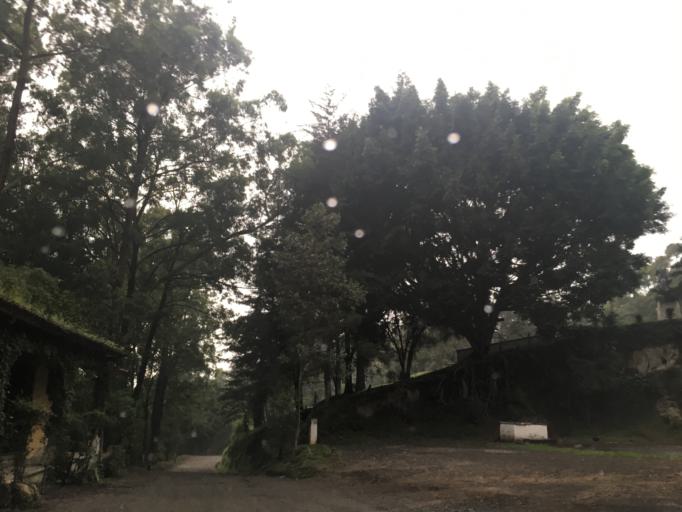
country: GT
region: Sacatepequez
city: Antigua Guatemala
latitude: 14.5669
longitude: -90.7301
